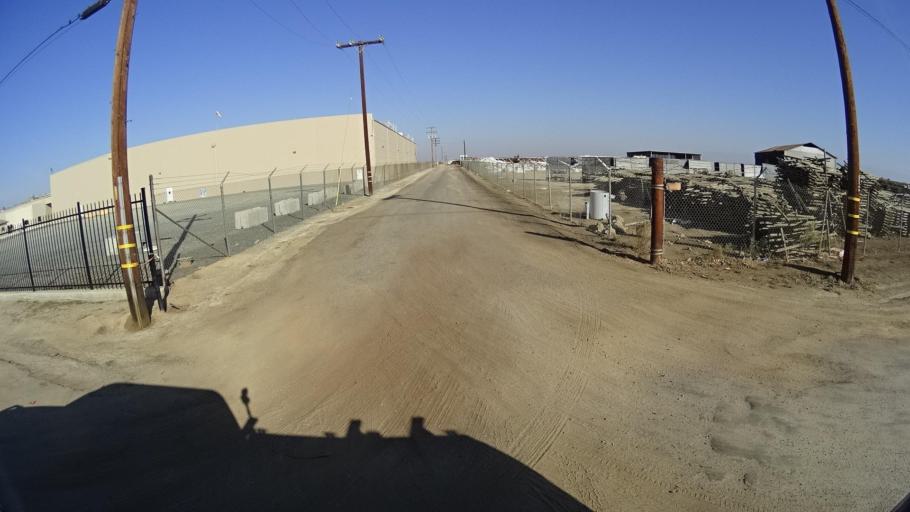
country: US
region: California
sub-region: Tulare County
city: Richgrove
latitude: 35.7471
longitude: -119.1429
